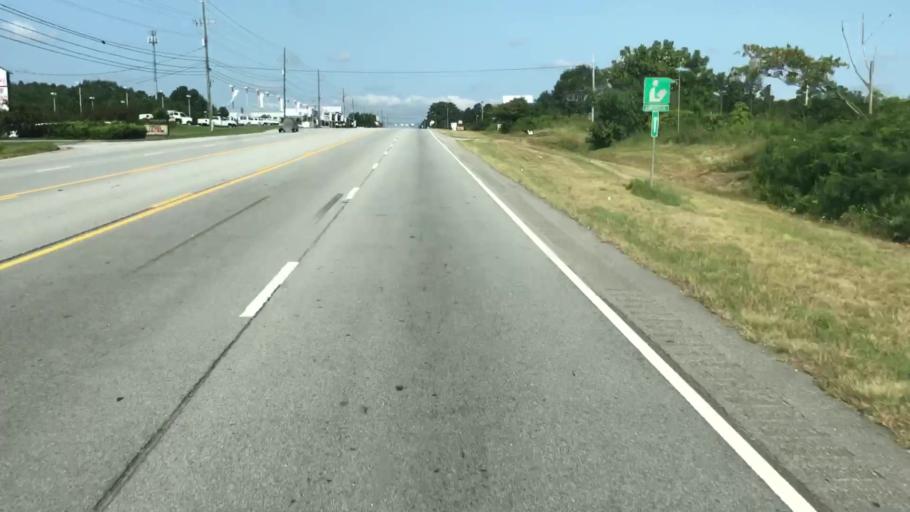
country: US
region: Georgia
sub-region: Walton County
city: Loganville
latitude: 33.8315
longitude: -83.8740
